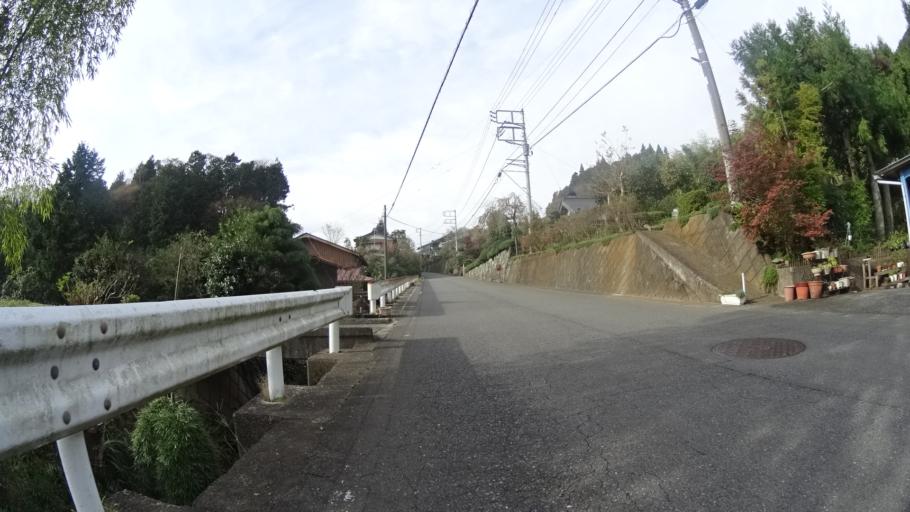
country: JP
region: Yamanashi
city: Uenohara
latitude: 35.6274
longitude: 139.0364
